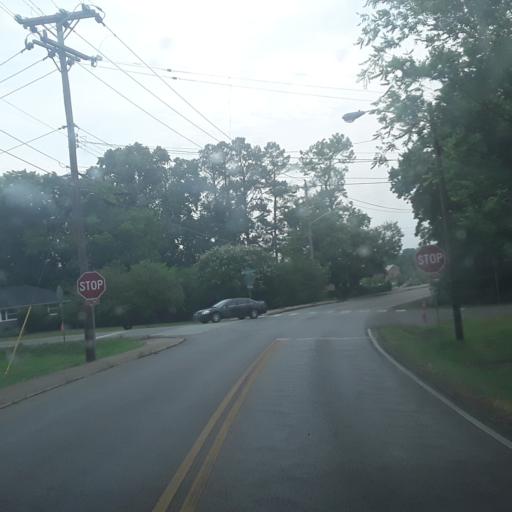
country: US
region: Tennessee
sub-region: Davidson County
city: Oak Hill
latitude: 36.0608
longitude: -86.7218
